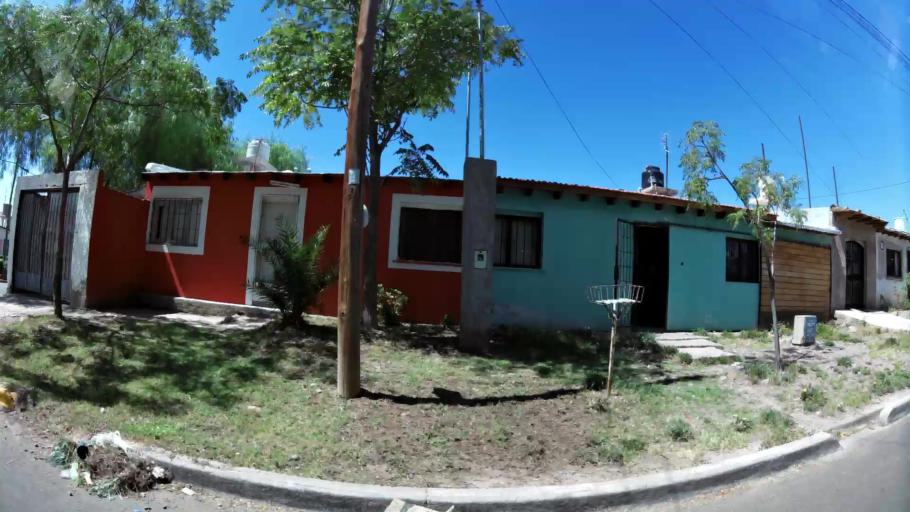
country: AR
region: Mendoza
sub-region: Departamento de Godoy Cruz
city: Godoy Cruz
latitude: -32.9477
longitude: -68.8689
